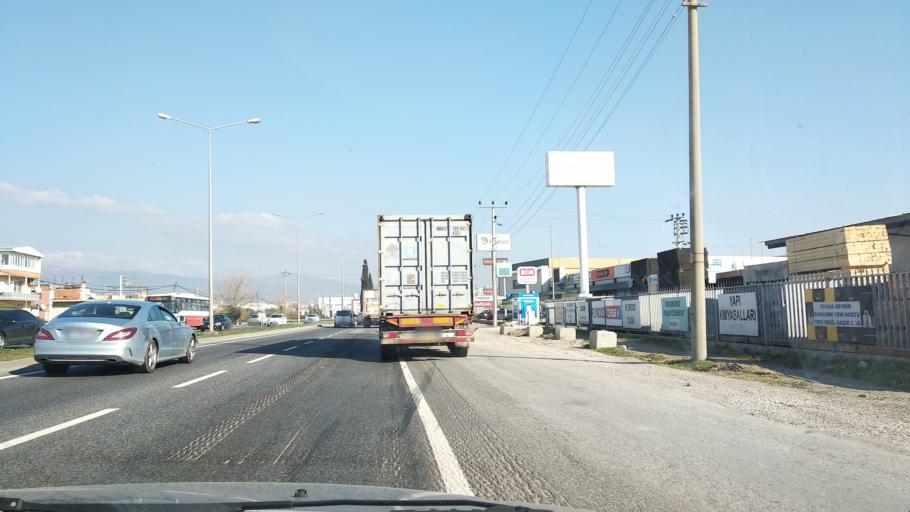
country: TR
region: Izmir
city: Menemen
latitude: 38.5780
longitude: 27.0645
